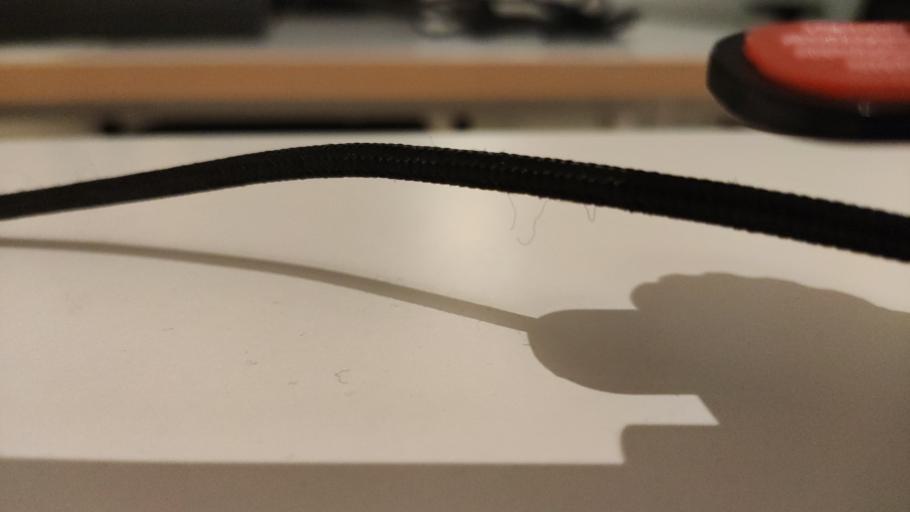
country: RU
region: Moskovskaya
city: Malino
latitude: 55.1103
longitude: 38.1424
